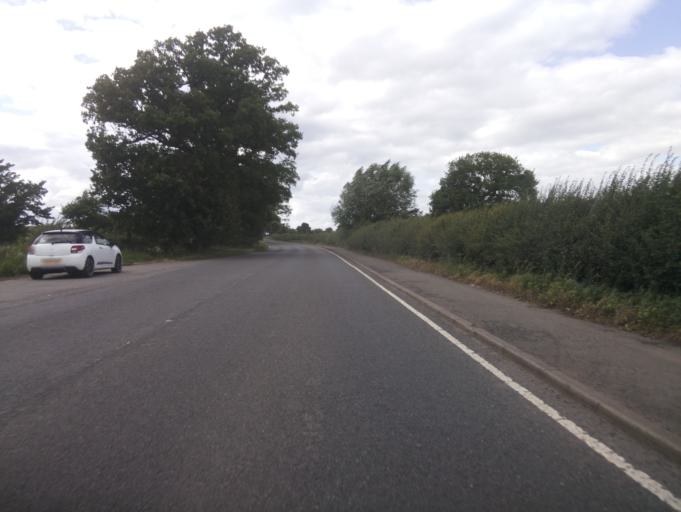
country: GB
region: England
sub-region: Warwickshire
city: Nuneaton
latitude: 52.5452
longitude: -1.4710
